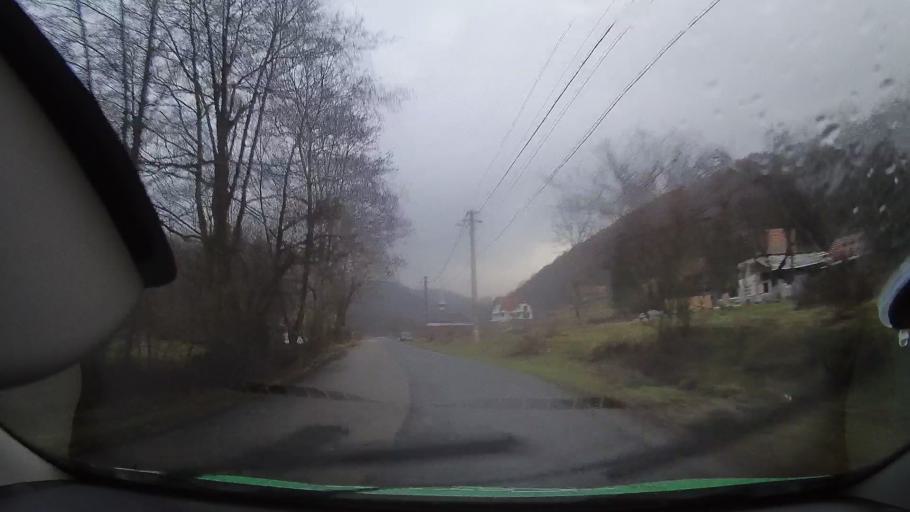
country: RO
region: Hunedoara
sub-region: Comuna Ribita
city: Ribita
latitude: 46.2576
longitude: 22.7464
